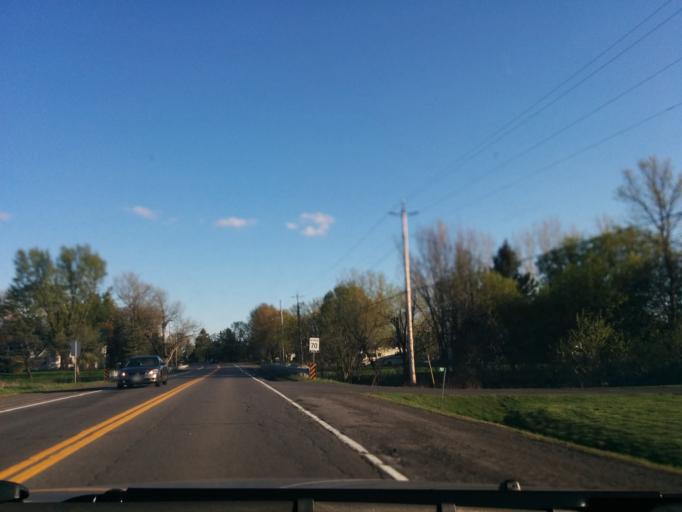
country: CA
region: Ontario
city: Bells Corners
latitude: 45.2571
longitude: -75.6992
